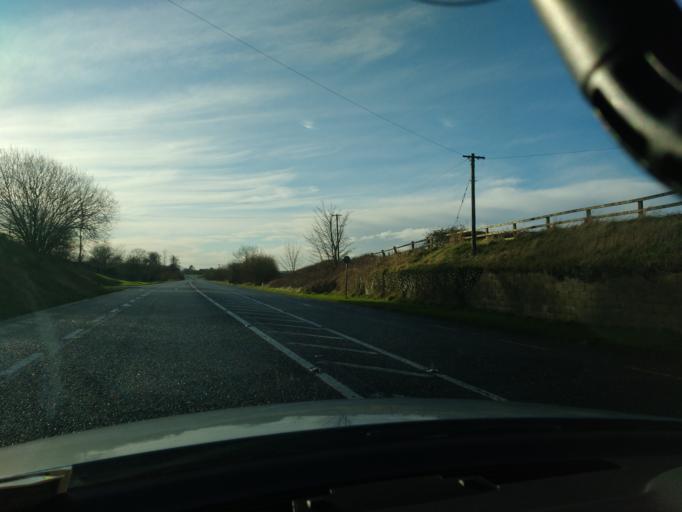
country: IE
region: Munster
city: Thurles
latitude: 52.6571
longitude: -7.7060
